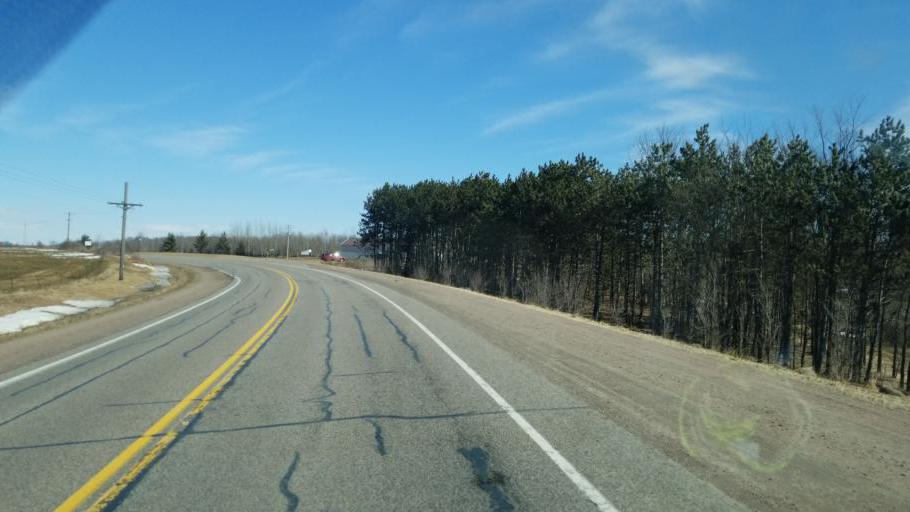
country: US
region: Wisconsin
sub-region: Clark County
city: Loyal
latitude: 44.5832
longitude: -90.3798
